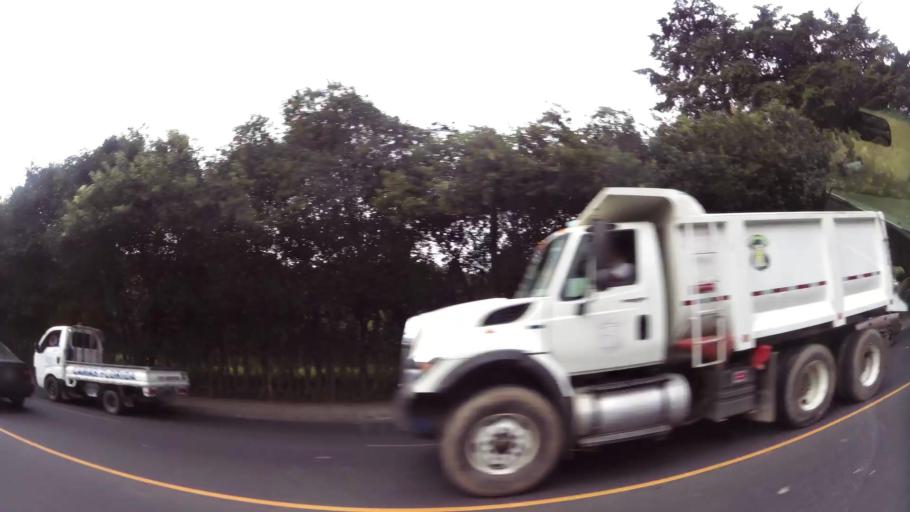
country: GT
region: Guatemala
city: Guatemala City
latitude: 14.6319
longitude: -90.5472
